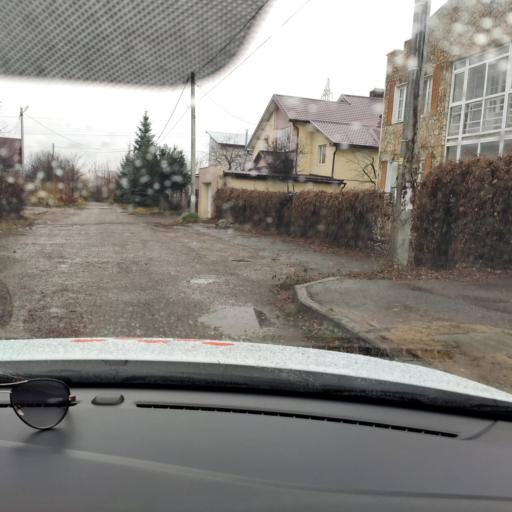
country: RU
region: Tatarstan
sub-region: Gorod Kazan'
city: Kazan
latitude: 55.8148
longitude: 49.2179
